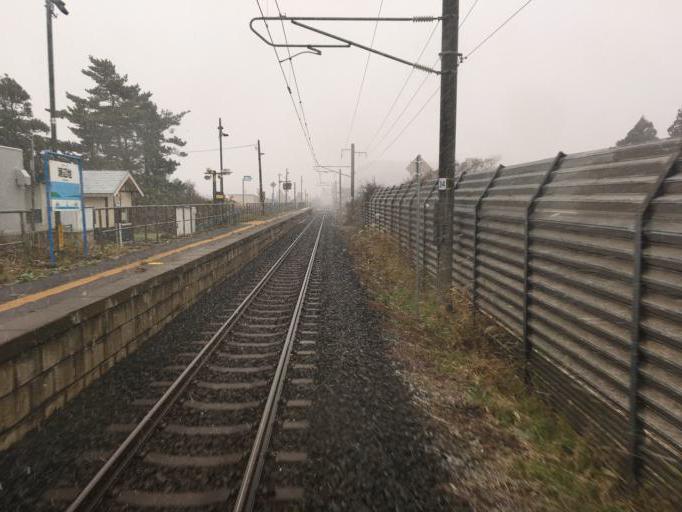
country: JP
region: Aomori
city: Aomori Shi
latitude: 41.0081
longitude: 140.6482
